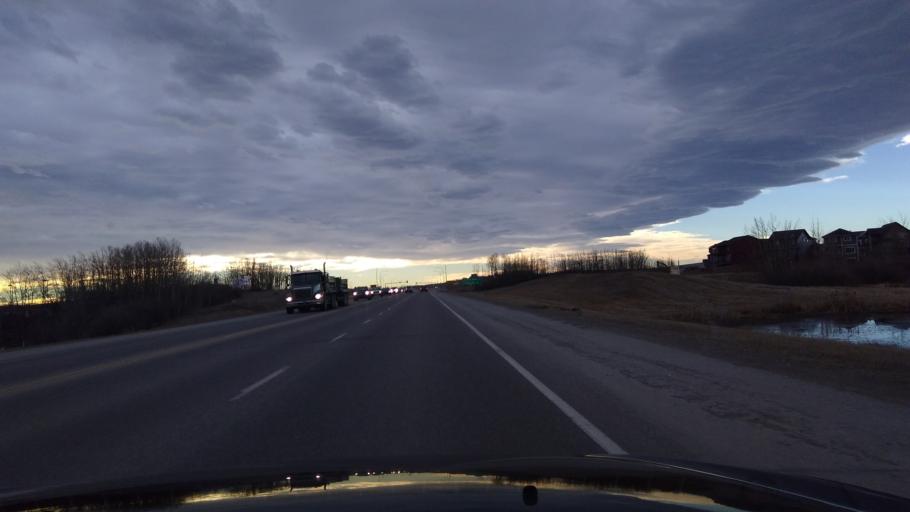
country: CA
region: Alberta
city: Cochrane
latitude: 51.1634
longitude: -114.4723
